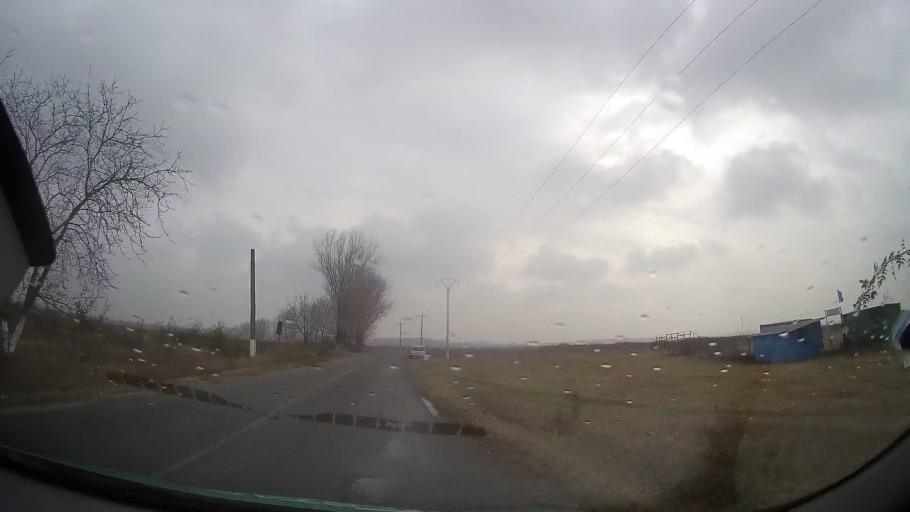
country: RO
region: Prahova
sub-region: Comuna Draganesti
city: Draganesti
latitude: 44.8362
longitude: 26.2697
